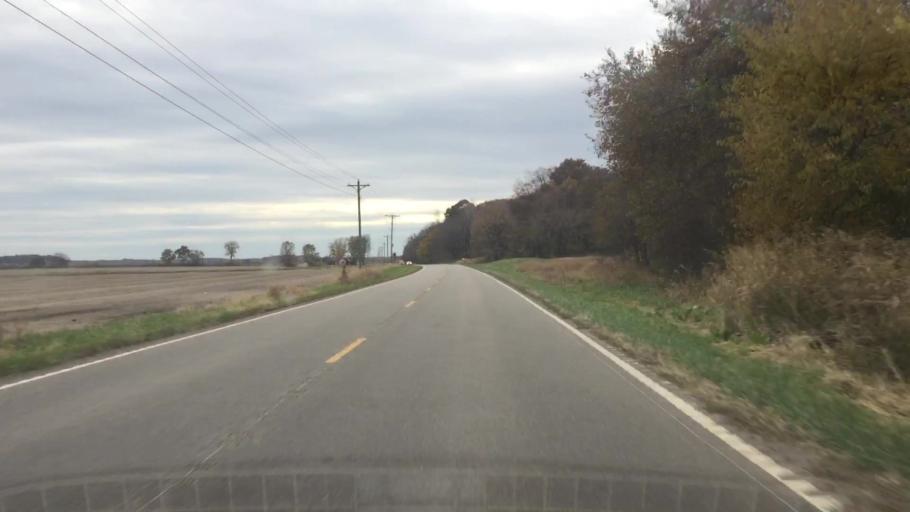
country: US
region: Missouri
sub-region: Callaway County
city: Holts Summit
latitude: 38.5956
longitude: -92.0114
